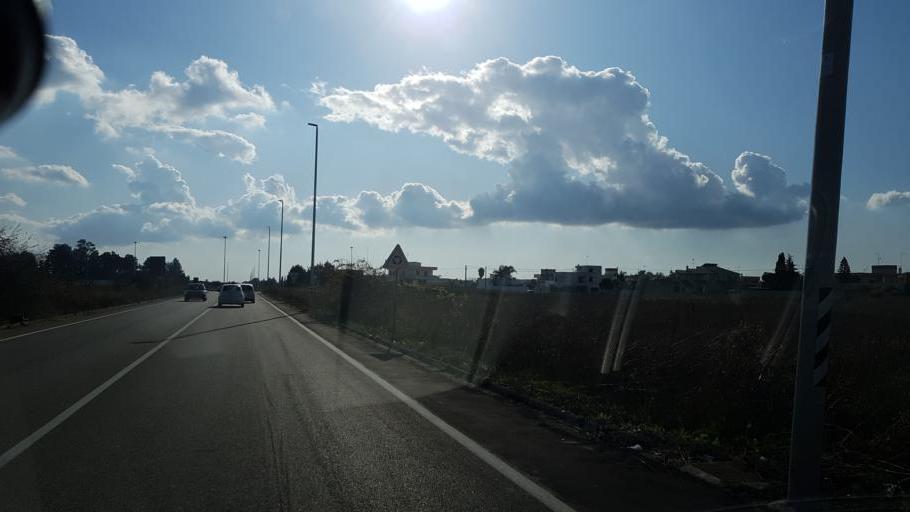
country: IT
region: Apulia
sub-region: Provincia di Lecce
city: Salice Salentino
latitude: 40.3825
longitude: 17.9702
